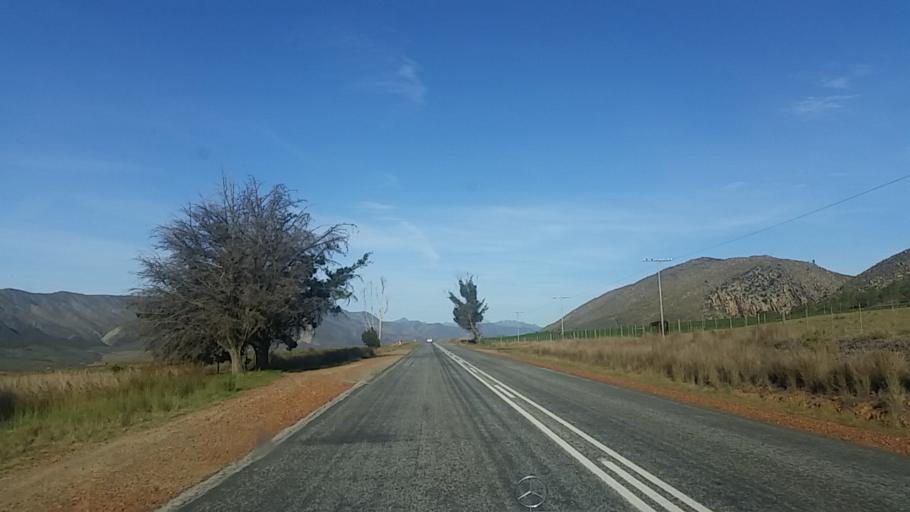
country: ZA
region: Western Cape
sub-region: Eden District Municipality
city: Knysna
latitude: -33.7724
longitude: 22.9428
